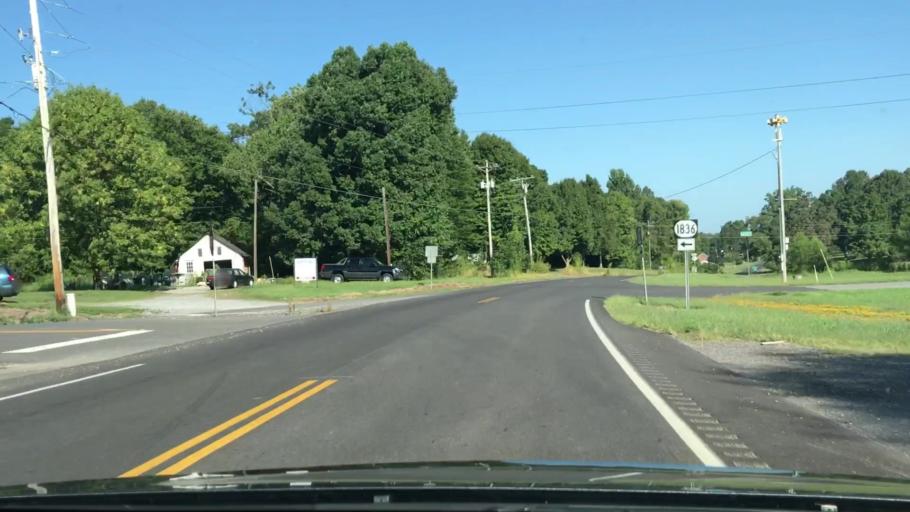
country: US
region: Kentucky
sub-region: Marshall County
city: Benton
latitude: 36.7694
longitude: -88.4388
